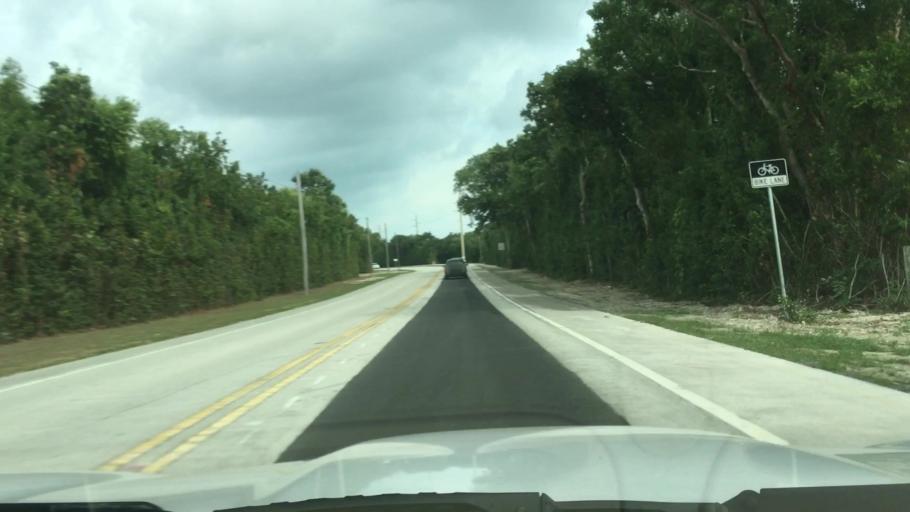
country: US
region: Florida
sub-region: Monroe County
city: North Key Largo
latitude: 25.2262
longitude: -80.3304
